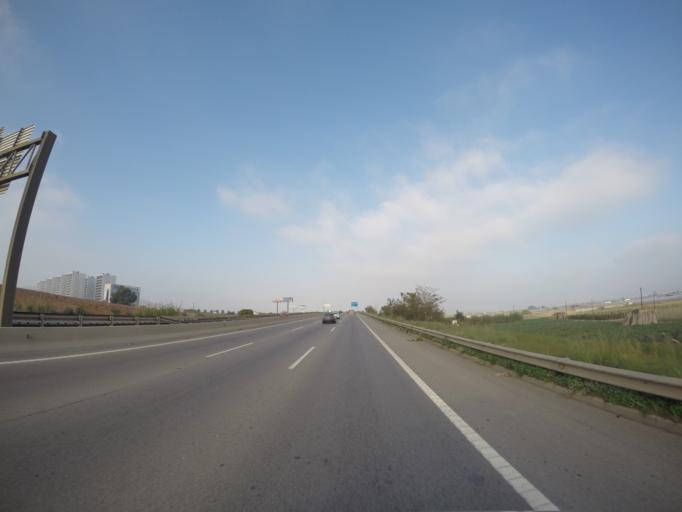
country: ES
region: Catalonia
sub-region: Provincia de Barcelona
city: Viladecans
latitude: 41.3075
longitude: 2.0285
